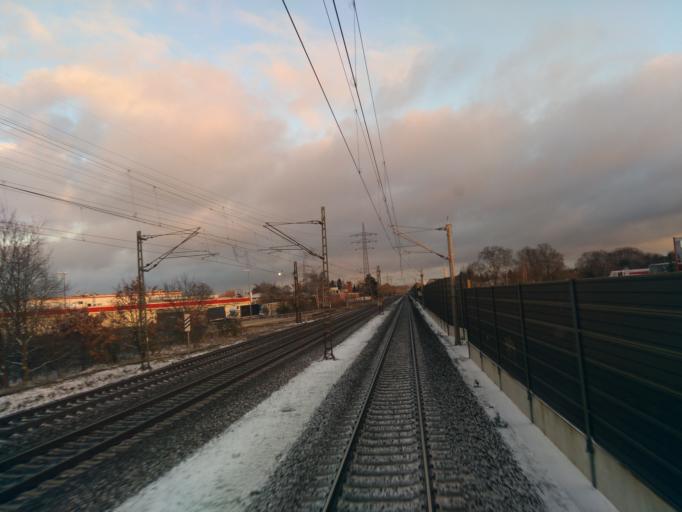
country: DE
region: Lower Saxony
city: Bardowick
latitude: 53.2737
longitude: 10.4020
